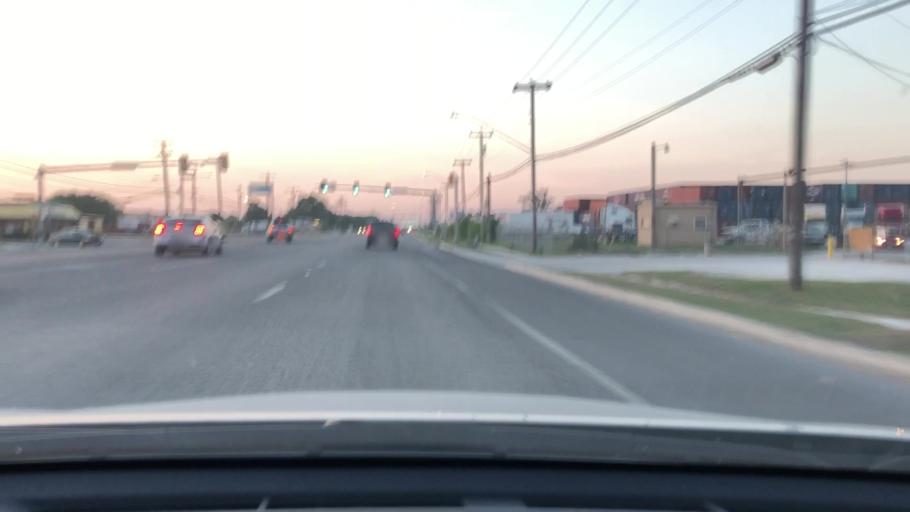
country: US
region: Texas
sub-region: Bexar County
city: Kirby
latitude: 29.4349
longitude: -98.4055
